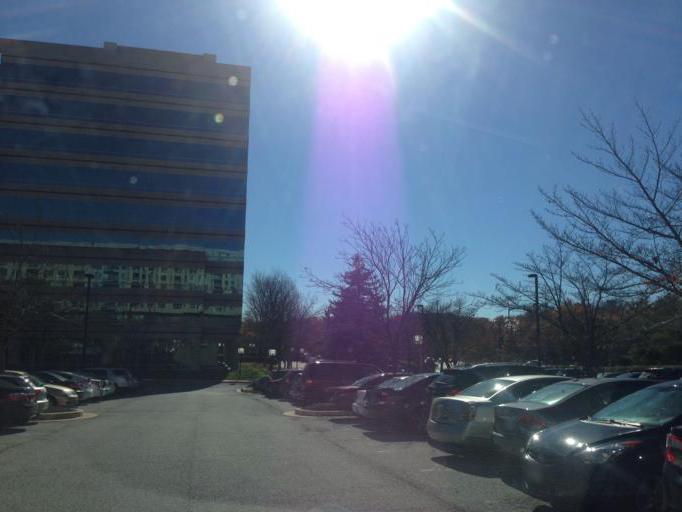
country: US
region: Maryland
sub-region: Howard County
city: Columbia
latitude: 39.2130
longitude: -76.8661
